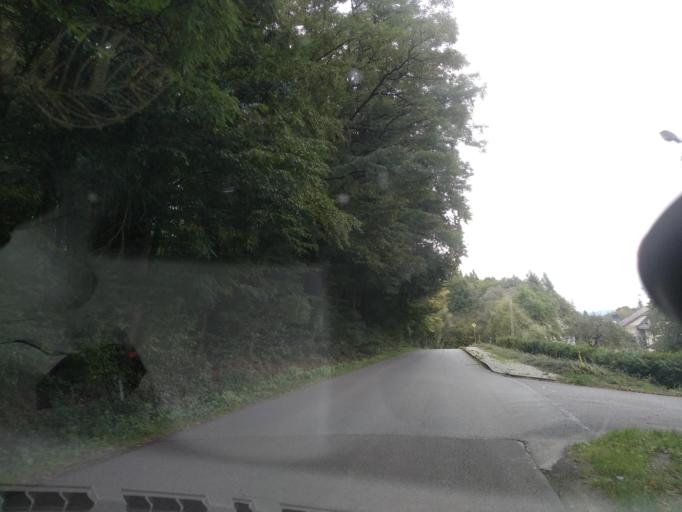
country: PL
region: Subcarpathian Voivodeship
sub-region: Powiat krosnienski
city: Miejsce Piastowe
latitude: 49.5984
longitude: 21.7525
